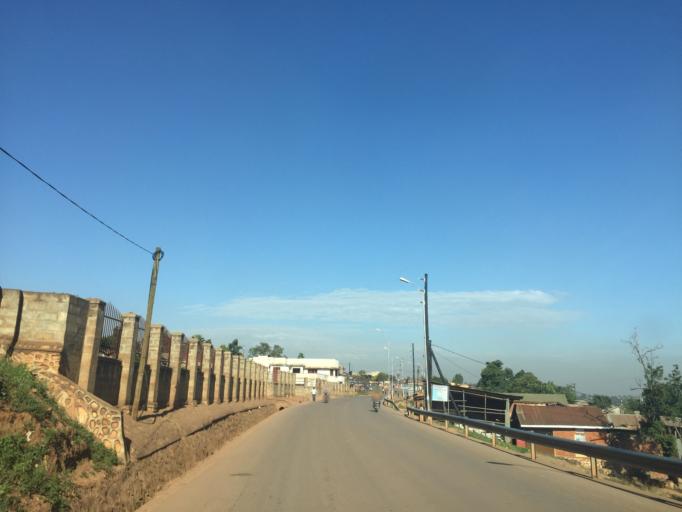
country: UG
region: Central Region
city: Kampala Central Division
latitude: 0.3814
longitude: 32.5628
